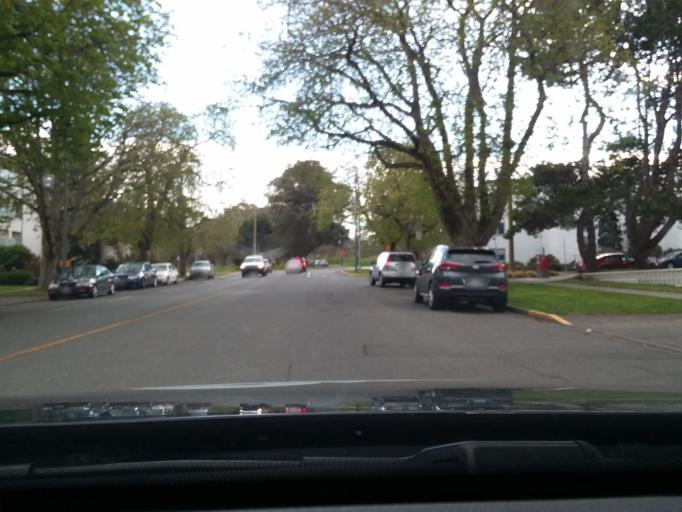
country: CA
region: British Columbia
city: Victoria
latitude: 48.4182
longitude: -123.3618
